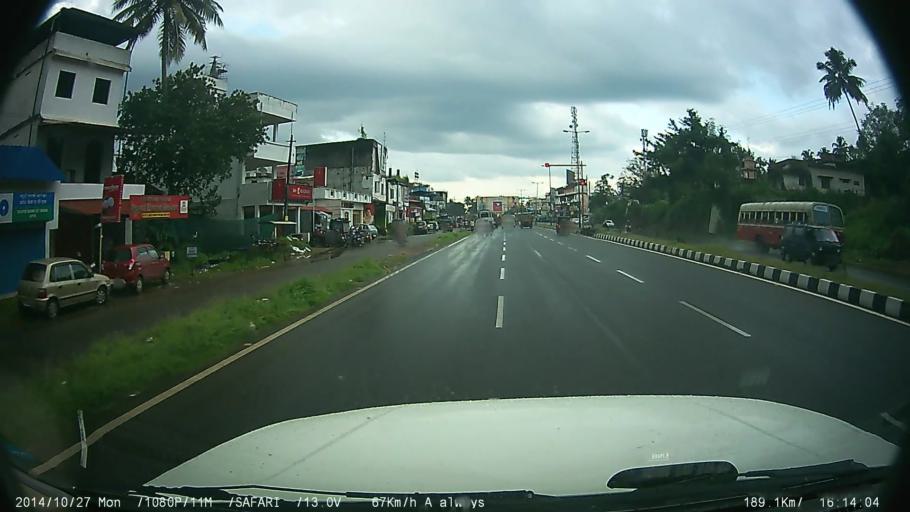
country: IN
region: Kerala
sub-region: Thrissur District
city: Irinjalakuda
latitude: 10.4205
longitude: 76.2700
